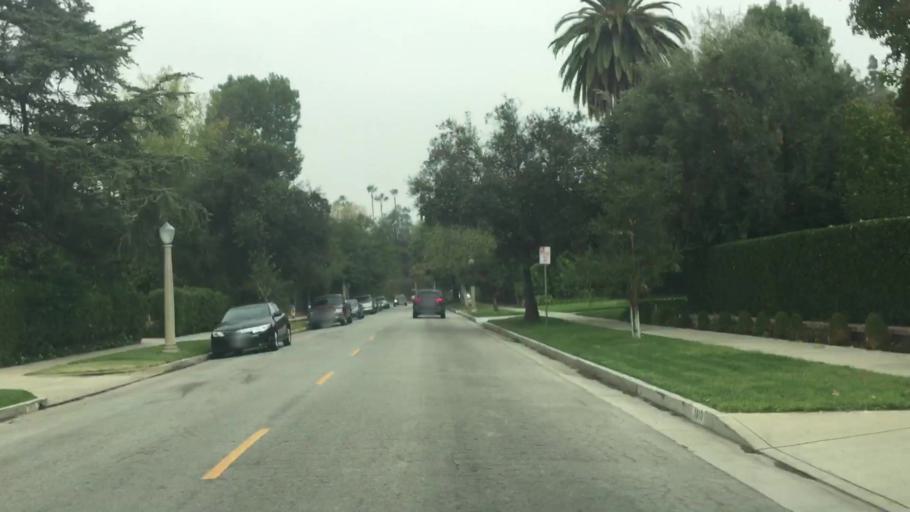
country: US
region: California
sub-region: Los Angeles County
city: Pasadena
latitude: 34.1295
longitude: -118.1291
